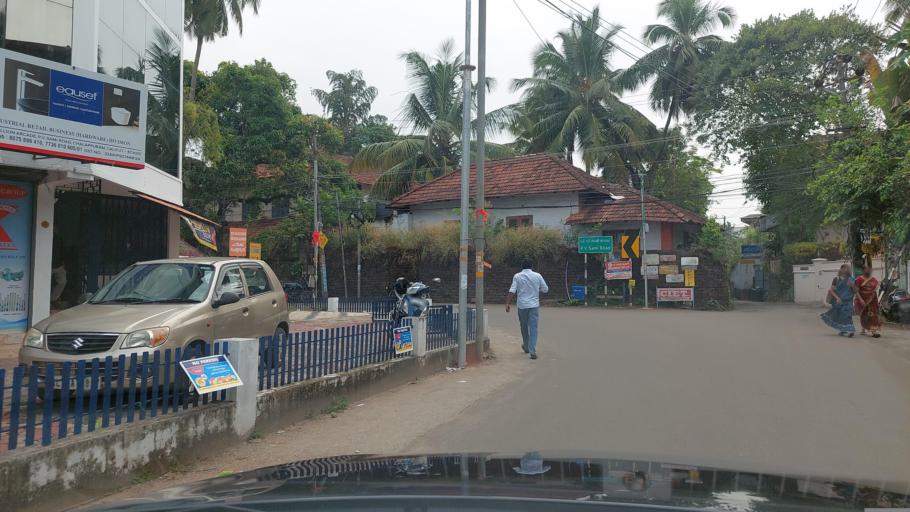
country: IN
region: Kerala
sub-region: Kozhikode
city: Kozhikode
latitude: 11.2456
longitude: 75.7872
